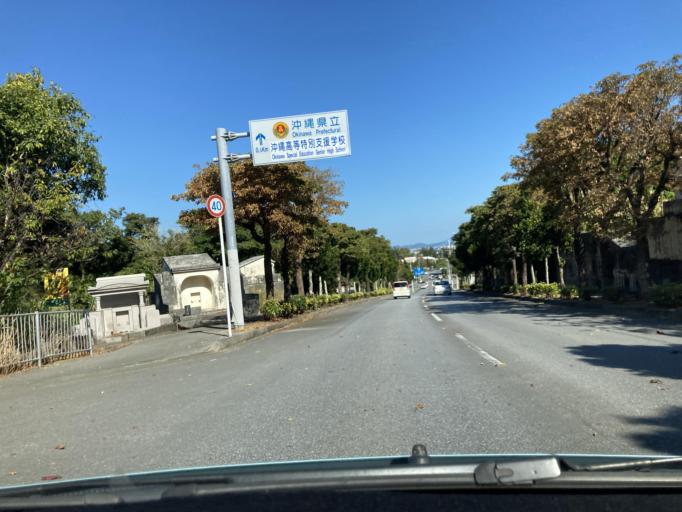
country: JP
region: Okinawa
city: Gushikawa
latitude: 26.3628
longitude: 127.8526
